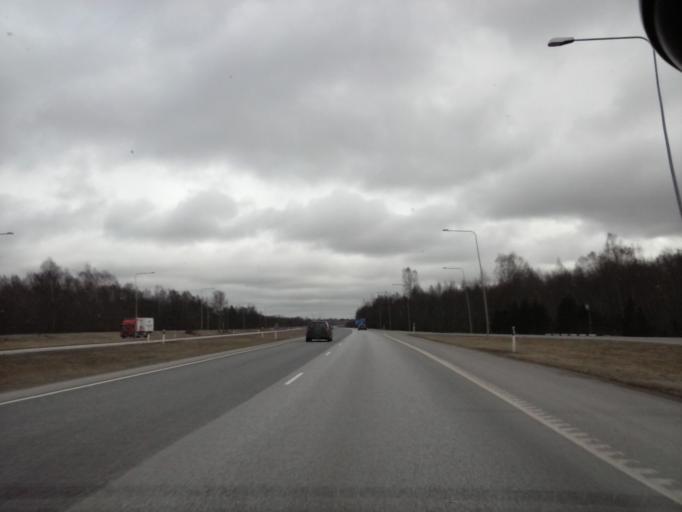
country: EE
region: Harju
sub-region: Rae vald
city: Vaida
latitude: 59.2990
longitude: 24.9515
